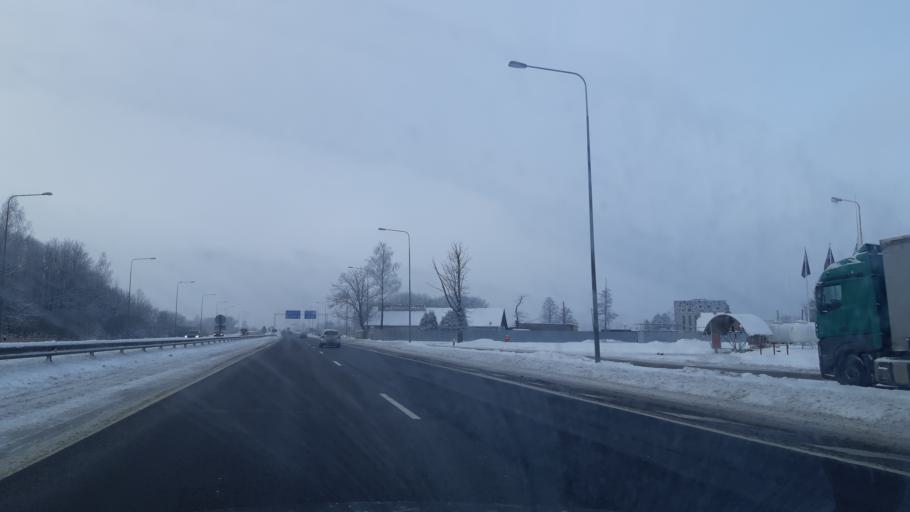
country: LT
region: Kauno apskritis
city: Dainava (Kaunas)
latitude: 54.9315
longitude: 23.9964
